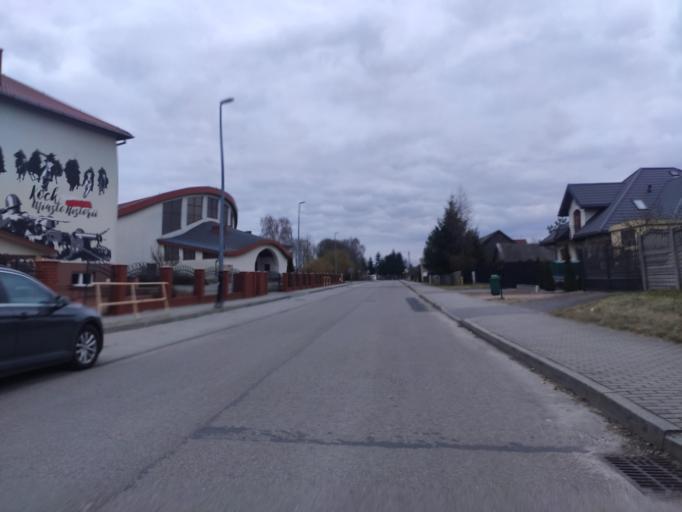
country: PL
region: Lublin Voivodeship
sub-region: Powiat lubartowski
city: Kock
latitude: 51.6408
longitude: 22.4358
